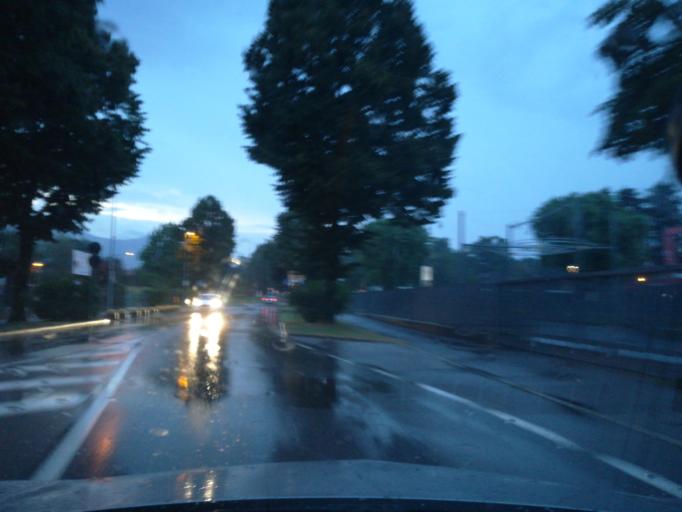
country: IT
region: Lombardy
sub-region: Provincia di Bergamo
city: Brembate di Sopra
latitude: 45.7184
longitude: 9.5817
